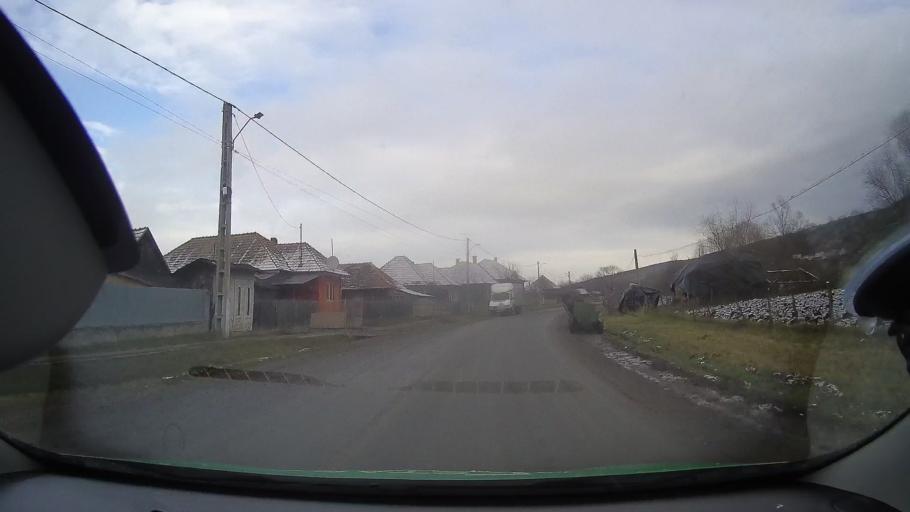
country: RO
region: Mures
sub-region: Comuna Ludus
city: Gheja
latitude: 46.3955
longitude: 24.0454
